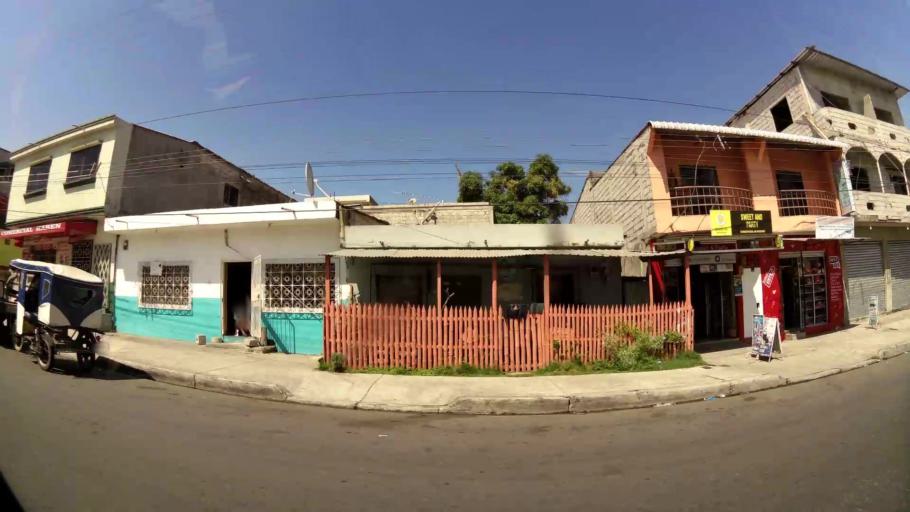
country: EC
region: Guayas
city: Guayaquil
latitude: -2.1261
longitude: -79.9206
